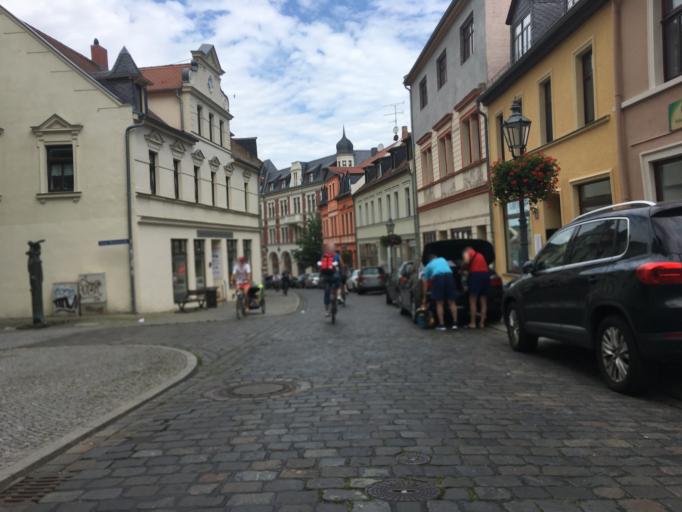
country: DE
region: Saxony-Anhalt
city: Bernburg
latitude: 51.7968
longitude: 11.7406
